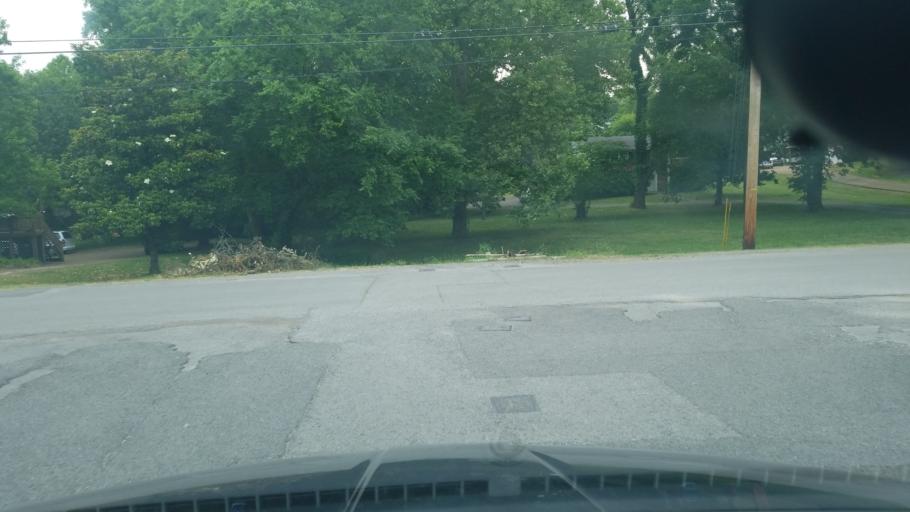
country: US
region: Tennessee
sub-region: Davidson County
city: Goodlettsville
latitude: 36.2591
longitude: -86.7401
